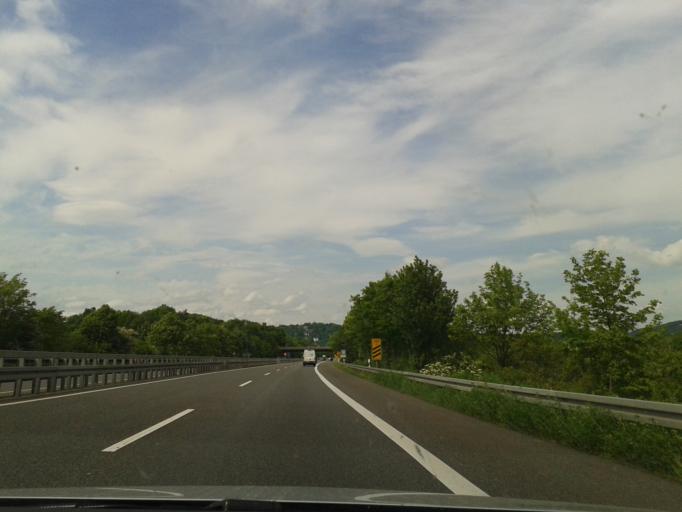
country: DE
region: Hesse
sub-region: Regierungsbezirk Giessen
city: Marburg an der Lahn
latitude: 50.7849
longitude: 8.7585
